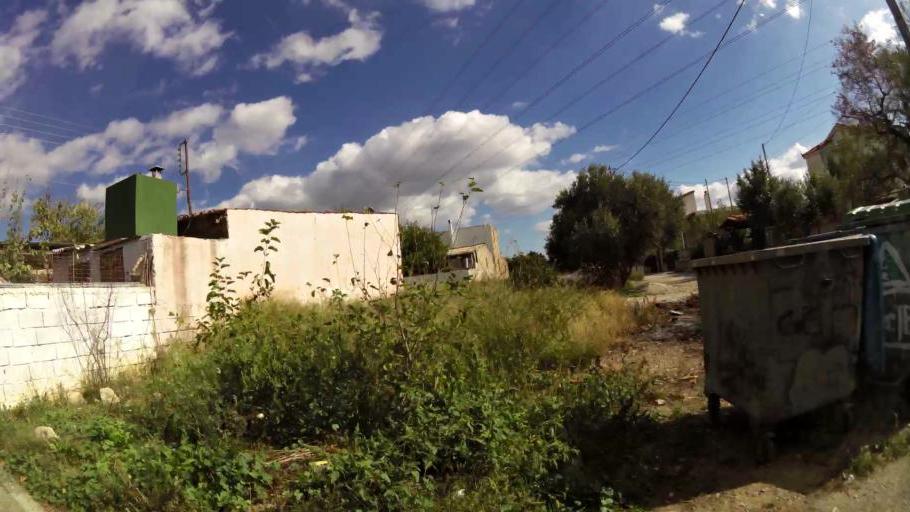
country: GR
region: Attica
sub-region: Nomarchia Anatolikis Attikis
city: Thrakomakedones
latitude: 38.1073
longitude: 23.7455
